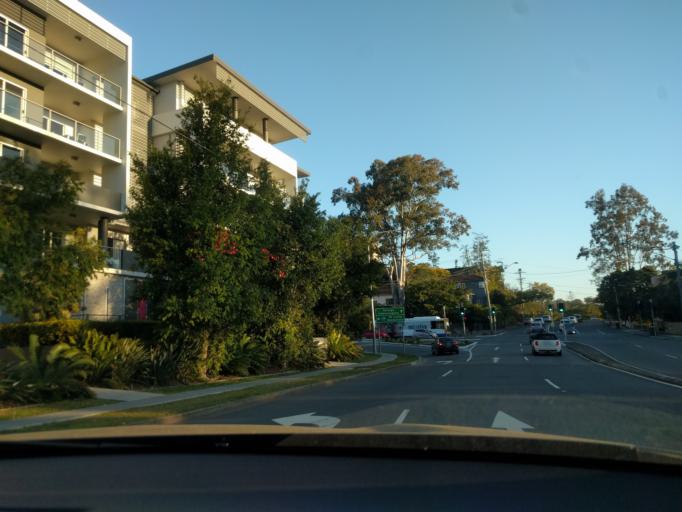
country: AU
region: Queensland
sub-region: Brisbane
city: Toowong
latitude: -27.4914
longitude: 152.9945
